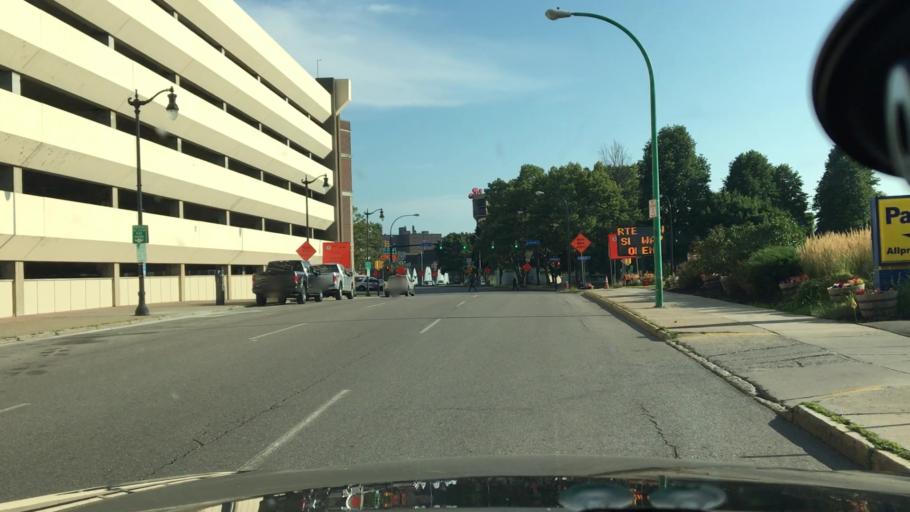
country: US
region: New York
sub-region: Erie County
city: Buffalo
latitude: 42.8861
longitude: -78.8800
